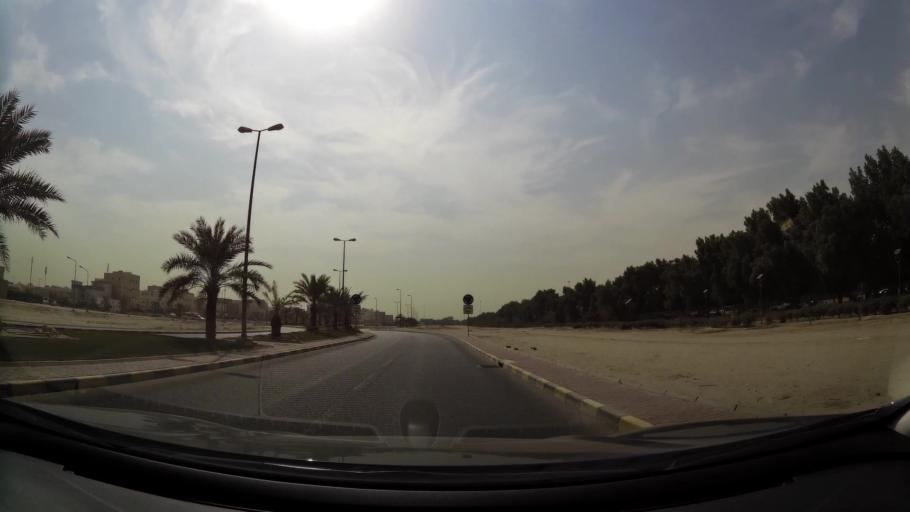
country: KW
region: Al Farwaniyah
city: Janub as Surrah
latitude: 29.2753
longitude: 47.9874
